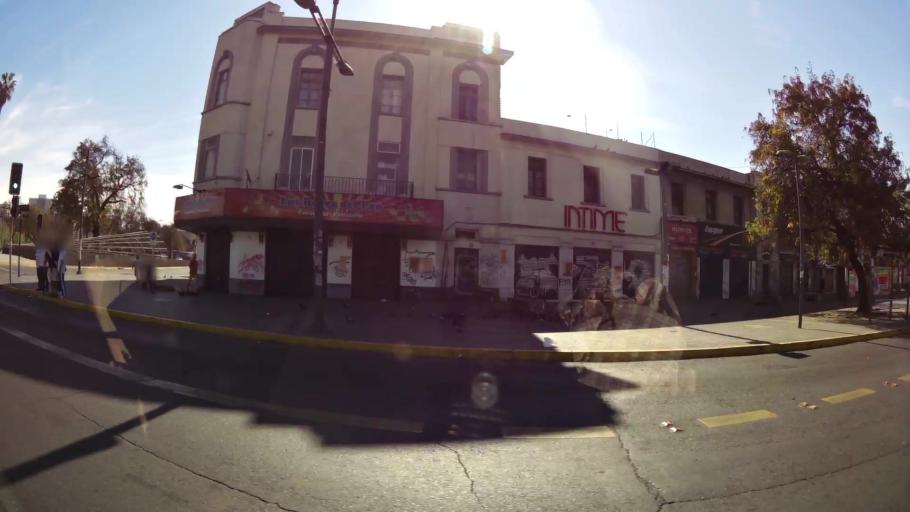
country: CL
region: Santiago Metropolitan
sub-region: Provincia de Santiago
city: Santiago
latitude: -33.4319
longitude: -70.6480
